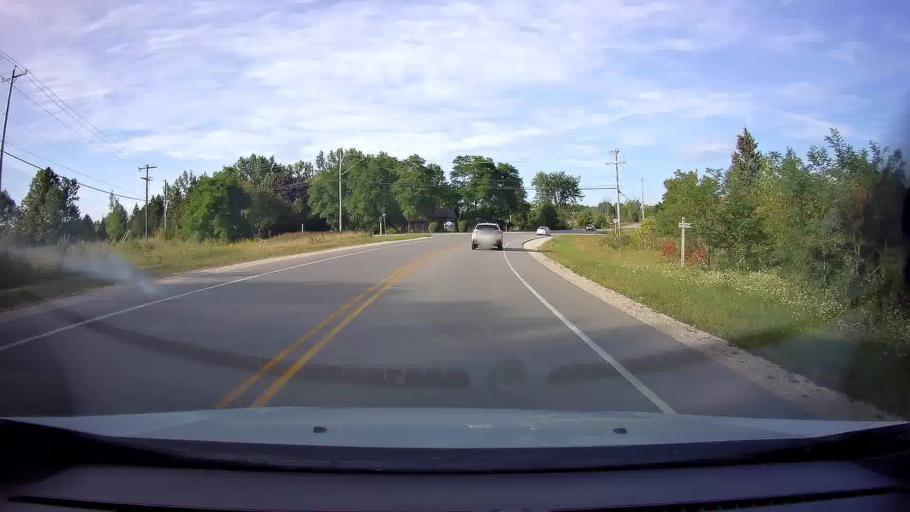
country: US
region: Wisconsin
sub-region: Door County
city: Sturgeon Bay
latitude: 45.1701
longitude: -87.1325
